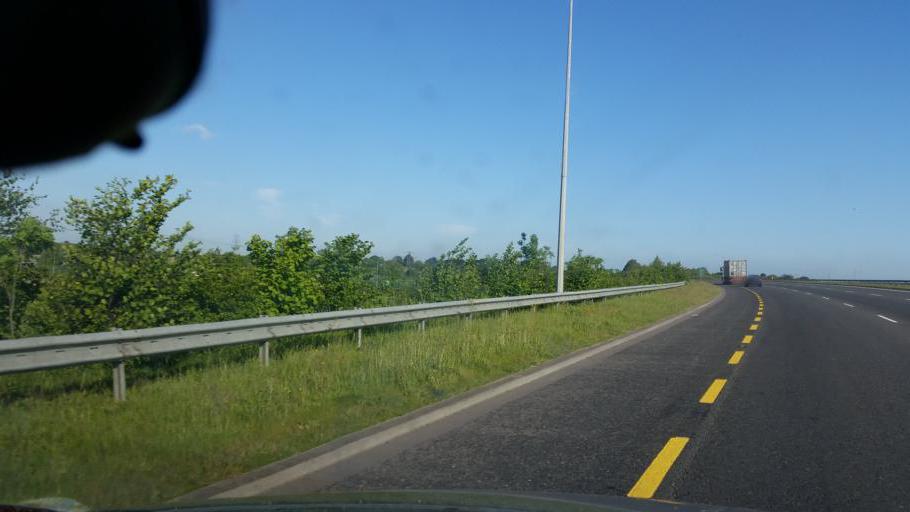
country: IE
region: Leinster
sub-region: Dublin City
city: Finglas
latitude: 53.4178
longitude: -6.3198
